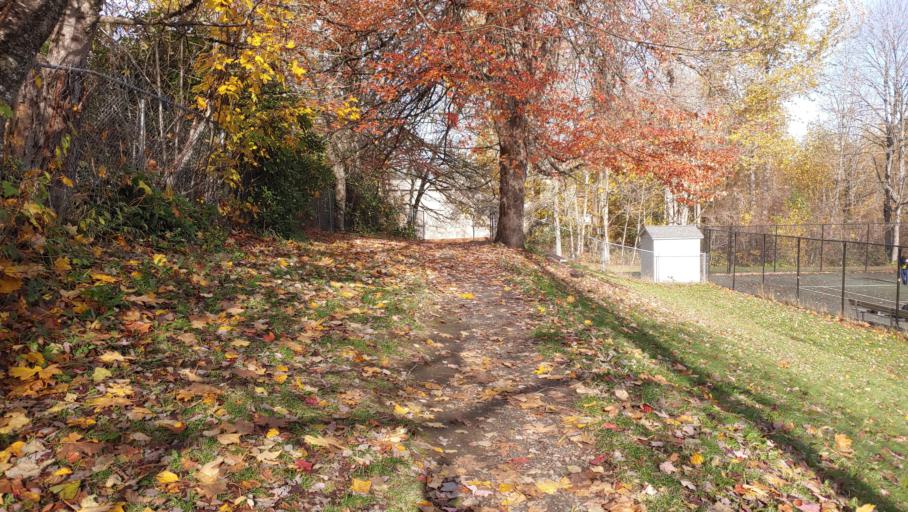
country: US
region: Washington
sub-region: King County
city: Fairwood
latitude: 47.4525
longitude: -122.1675
